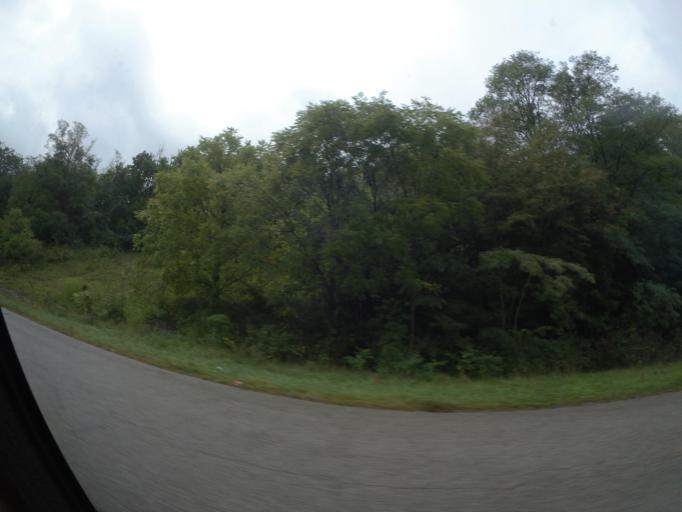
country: US
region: Indiana
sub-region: Montgomery County
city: Crawfordsville
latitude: 40.0571
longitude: -86.9083
